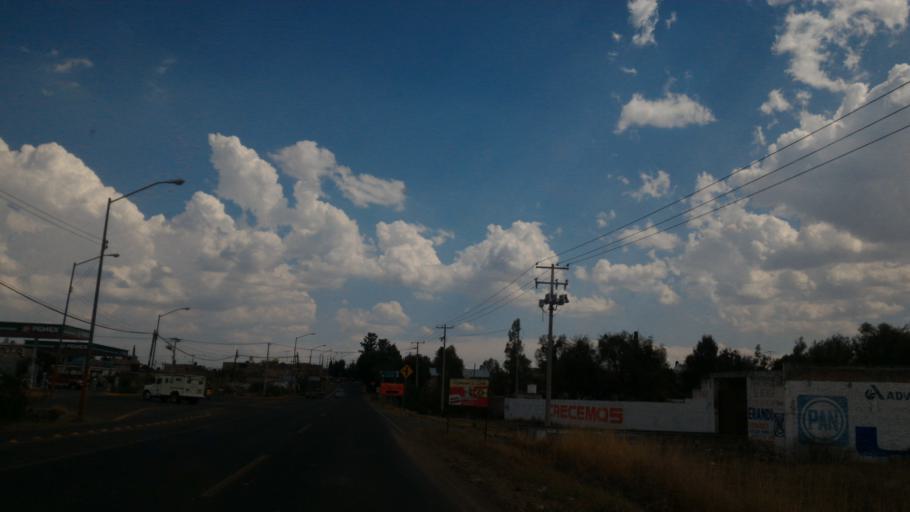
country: MX
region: Guanajuato
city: Ciudad Manuel Doblado
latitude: 20.7386
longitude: -101.9542
